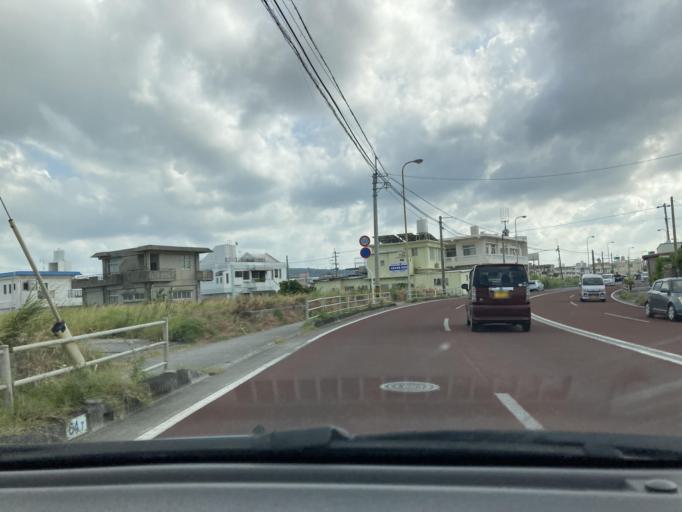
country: JP
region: Okinawa
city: Ginowan
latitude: 26.2165
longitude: 127.7638
